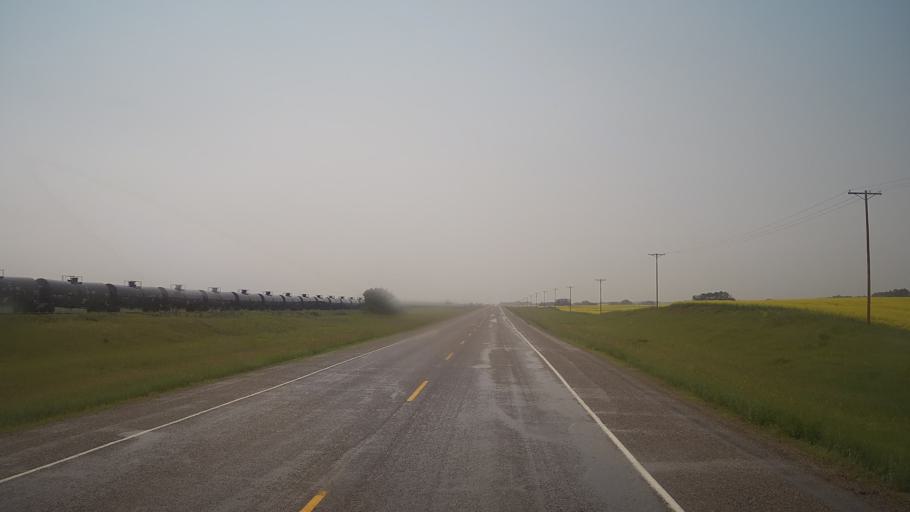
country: CA
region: Saskatchewan
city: Biggar
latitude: 52.1594
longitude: -108.2728
